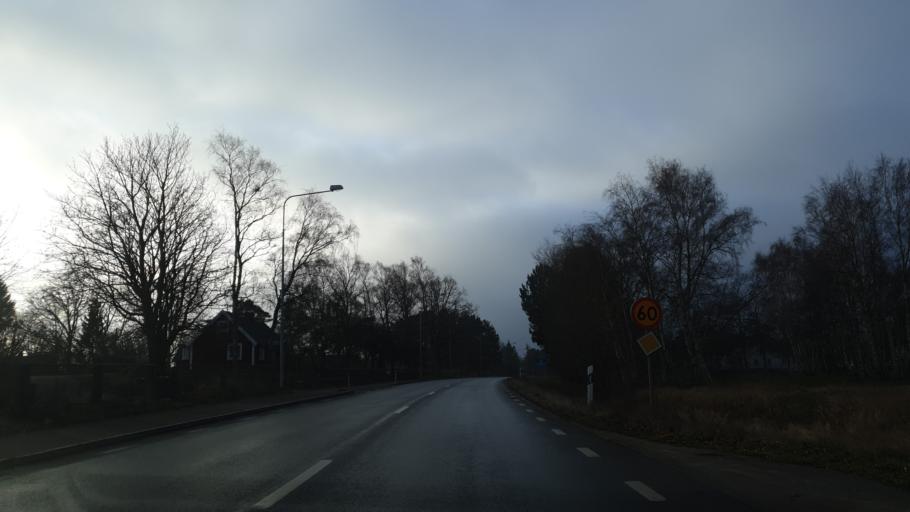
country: SE
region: Blekinge
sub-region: Karlshamns Kommun
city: Morrum
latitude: 56.1592
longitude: 14.6787
